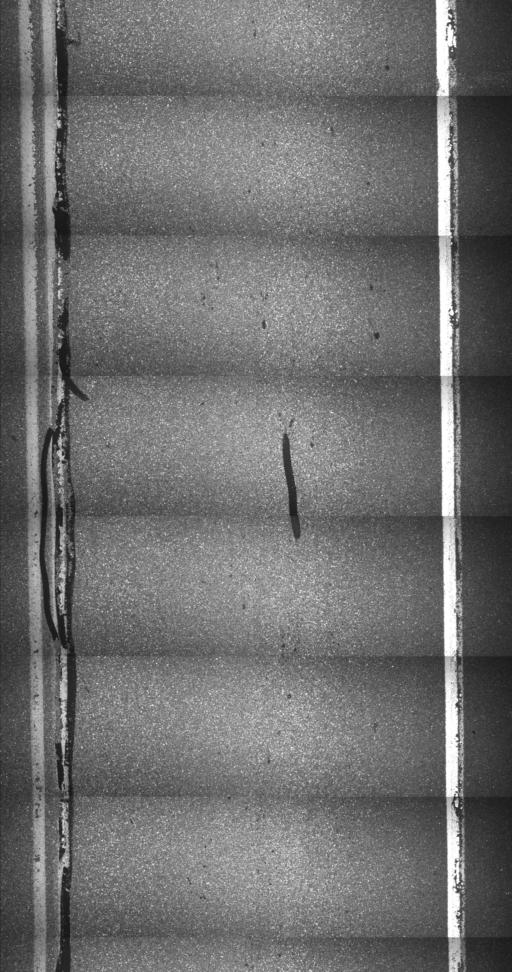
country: CA
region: Quebec
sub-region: Estrie
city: Coaticook
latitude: 44.9460
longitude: -71.8478
